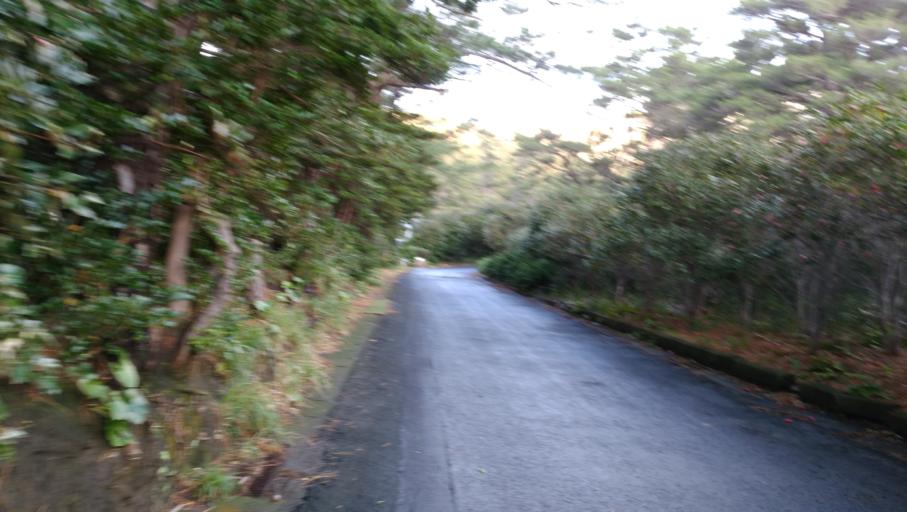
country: JP
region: Kagoshima
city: Makurazaki
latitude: 30.7835
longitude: 130.2799
